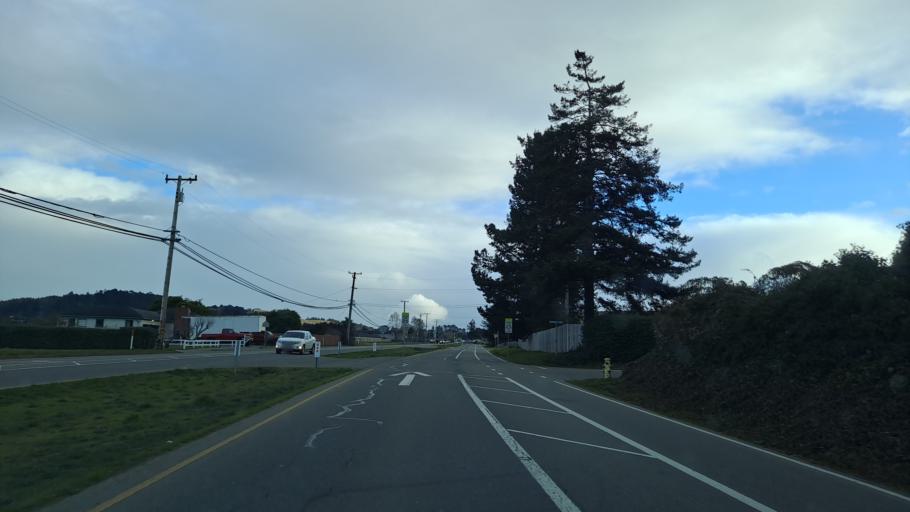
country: US
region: California
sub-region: Humboldt County
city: Fortuna
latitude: 40.5747
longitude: -124.1440
